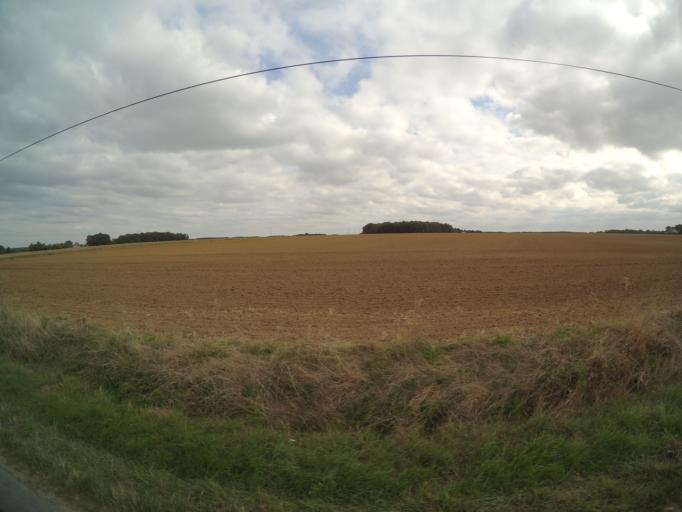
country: FR
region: Centre
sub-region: Departement d'Indre-et-Loire
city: Nazelles-Negron
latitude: 47.4837
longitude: 0.9470
